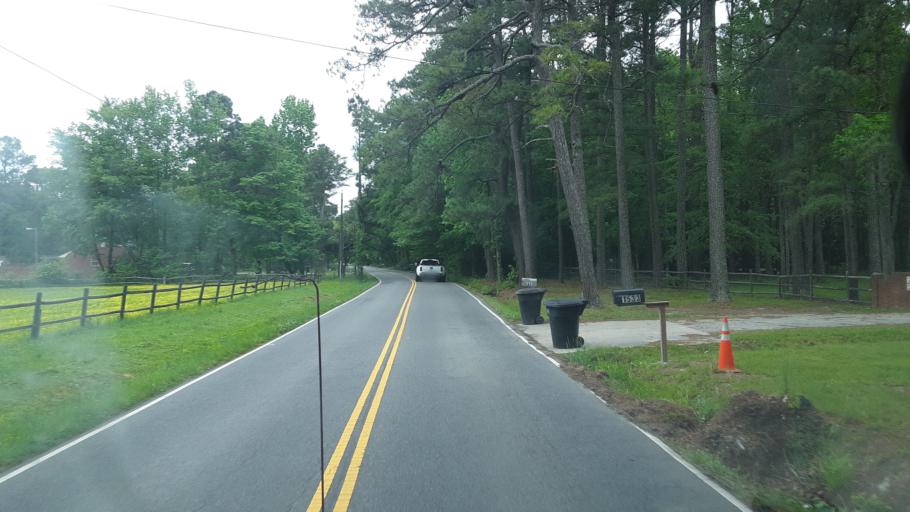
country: US
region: Virginia
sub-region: City of Virginia Beach
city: Virginia Beach
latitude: 36.7382
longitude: -75.9888
